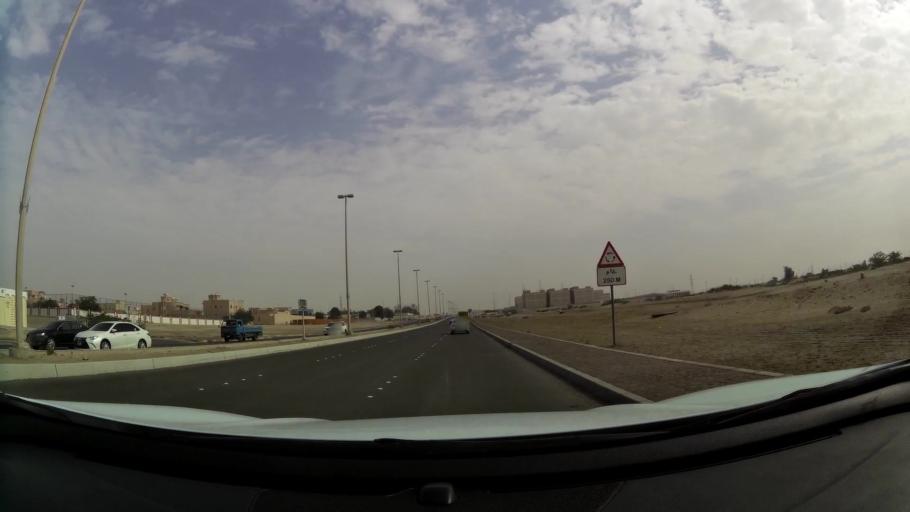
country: AE
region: Abu Dhabi
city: Abu Dhabi
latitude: 24.2901
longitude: 54.6562
